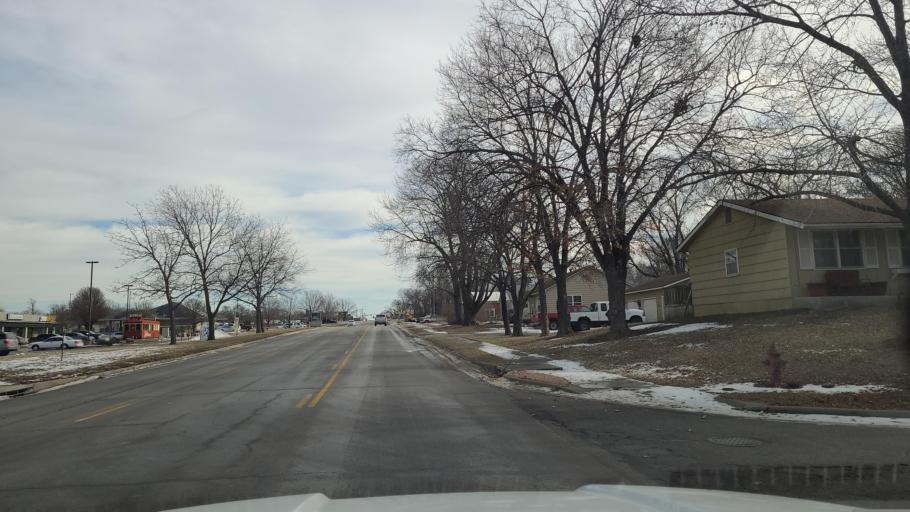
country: US
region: Kansas
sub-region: Douglas County
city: Baldwin City
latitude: 38.7822
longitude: -95.1917
